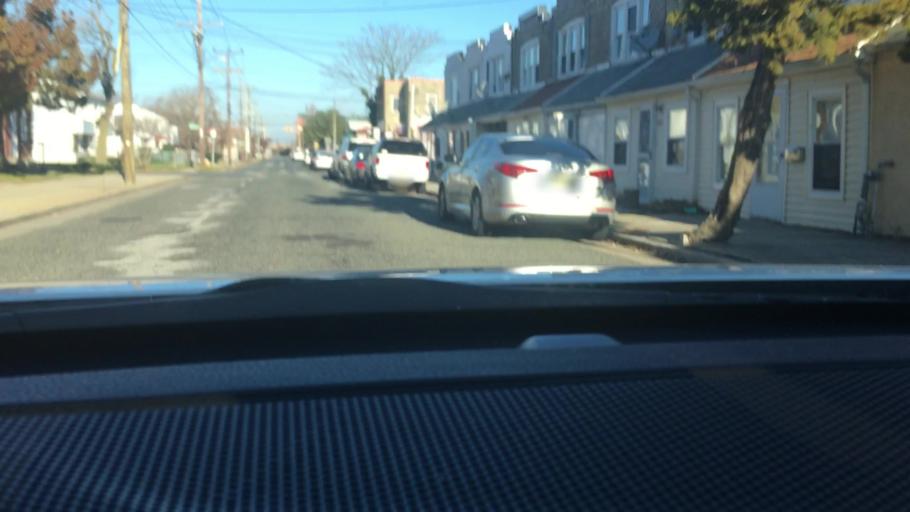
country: US
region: New Jersey
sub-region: Atlantic County
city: Atlantic City
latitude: 39.3686
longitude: -74.4340
